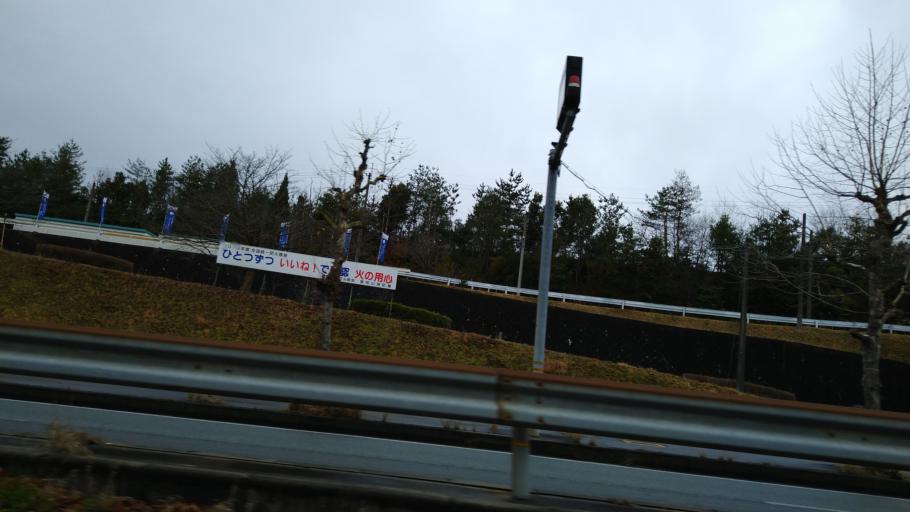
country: JP
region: Kyoto
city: Fukuchiyama
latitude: 35.2773
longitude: 135.1825
